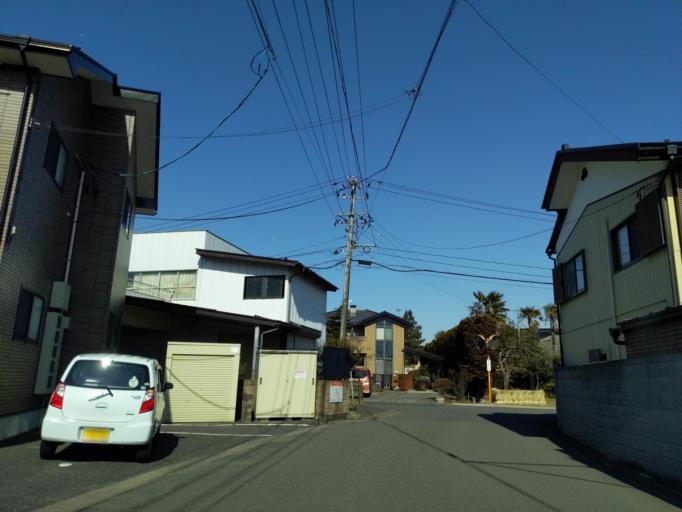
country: JP
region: Fukushima
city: Koriyama
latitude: 37.4256
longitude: 140.3553
